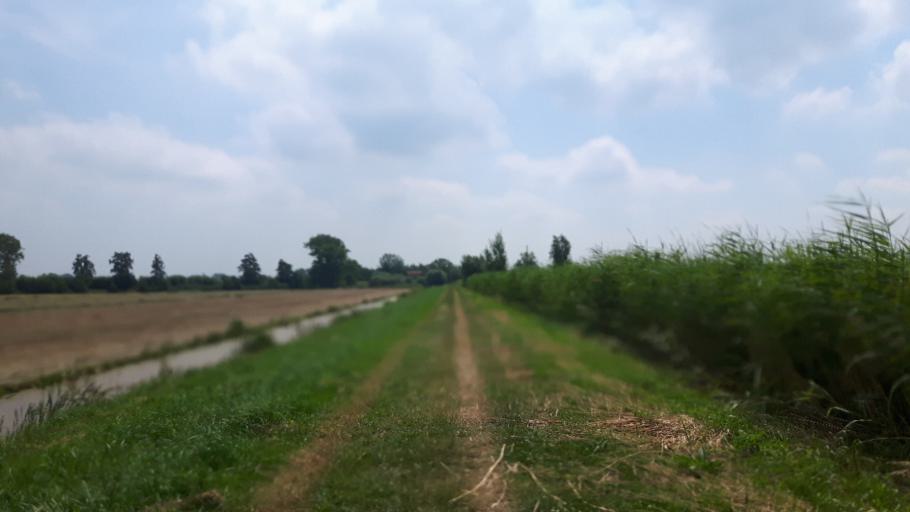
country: NL
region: Utrecht
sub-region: Gemeente Lopik
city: Lopik
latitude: 51.9466
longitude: 4.9958
